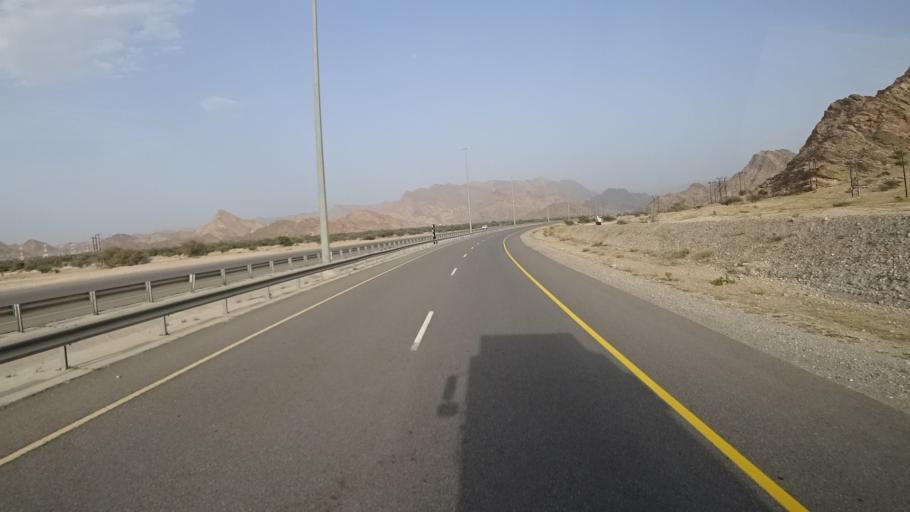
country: OM
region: Muhafazat Masqat
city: Muscat
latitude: 23.3683
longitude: 58.6424
